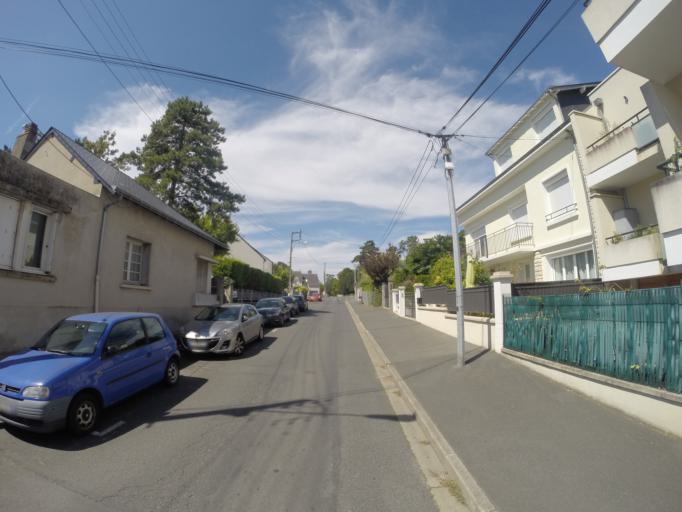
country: FR
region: Centre
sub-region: Departement d'Indre-et-Loire
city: Tours
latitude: 47.4095
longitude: 0.7120
